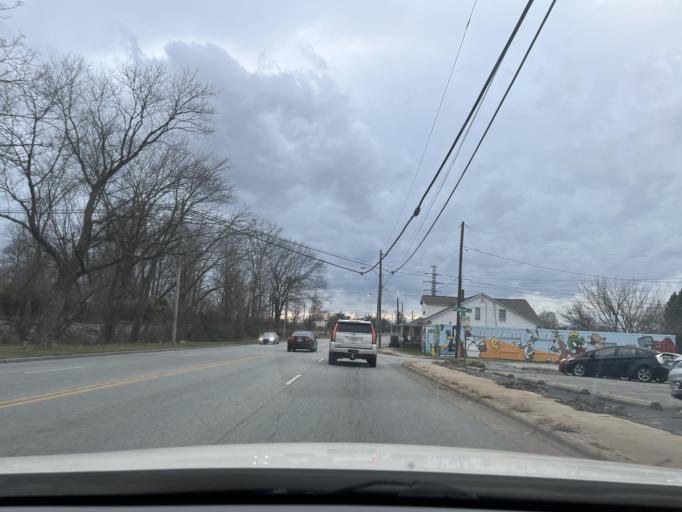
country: US
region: North Carolina
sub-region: Guilford County
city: Greensboro
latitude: 36.0612
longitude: -79.8571
